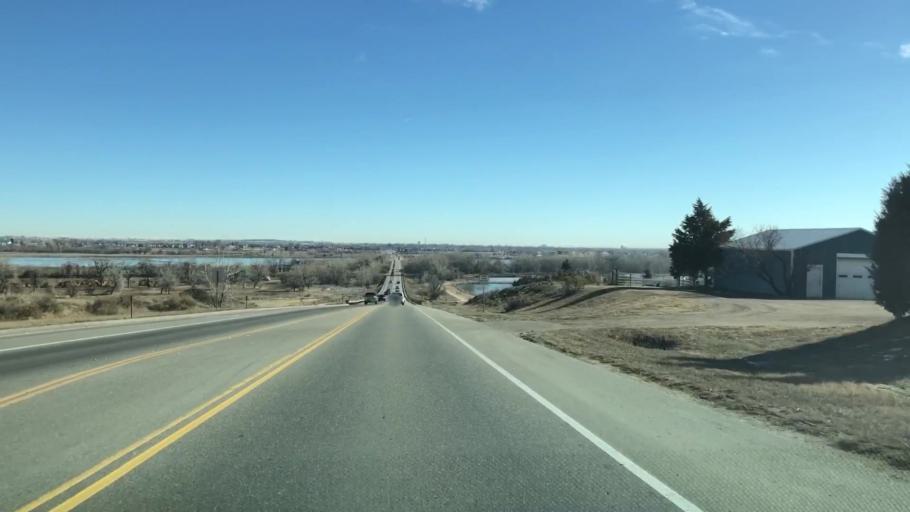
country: US
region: Colorado
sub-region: Weld County
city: Windsor
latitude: 40.4793
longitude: -104.9624
